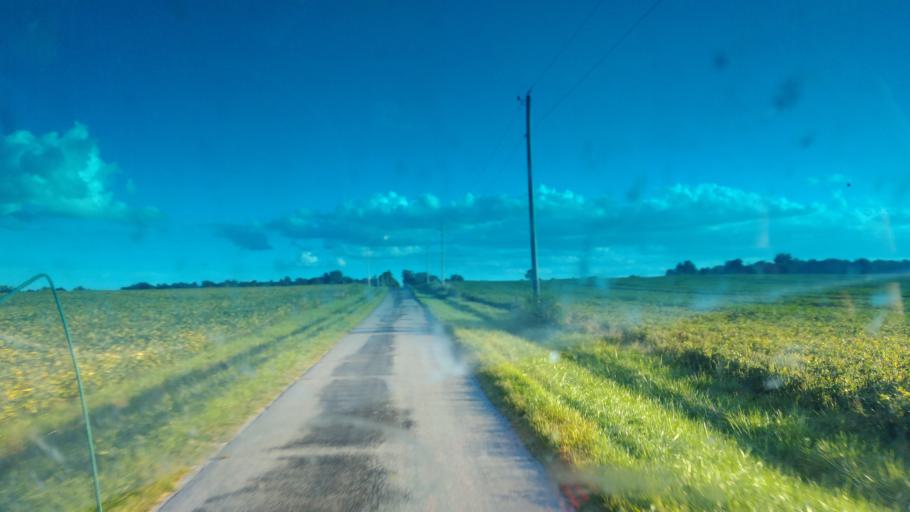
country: US
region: Ohio
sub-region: Wyandot County
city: Upper Sandusky
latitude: 40.8835
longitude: -83.1509
